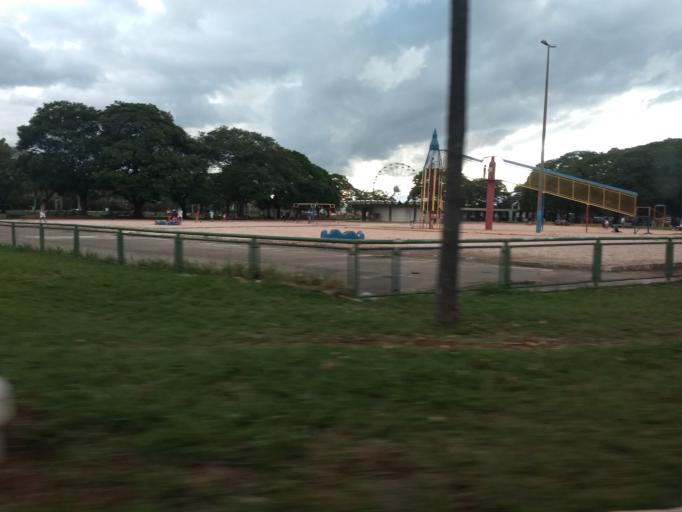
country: BR
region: Federal District
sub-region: Brasilia
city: Brasilia
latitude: -15.7935
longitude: -47.8951
